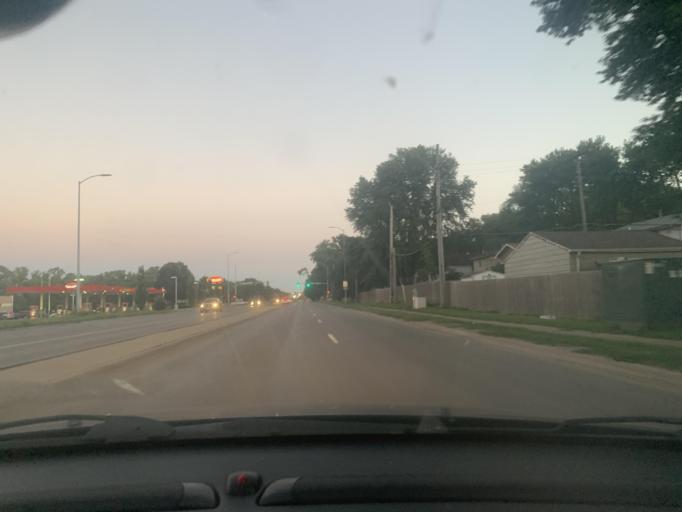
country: US
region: Nebraska
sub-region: Douglas County
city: Ralston
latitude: 41.2999
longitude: -96.0527
